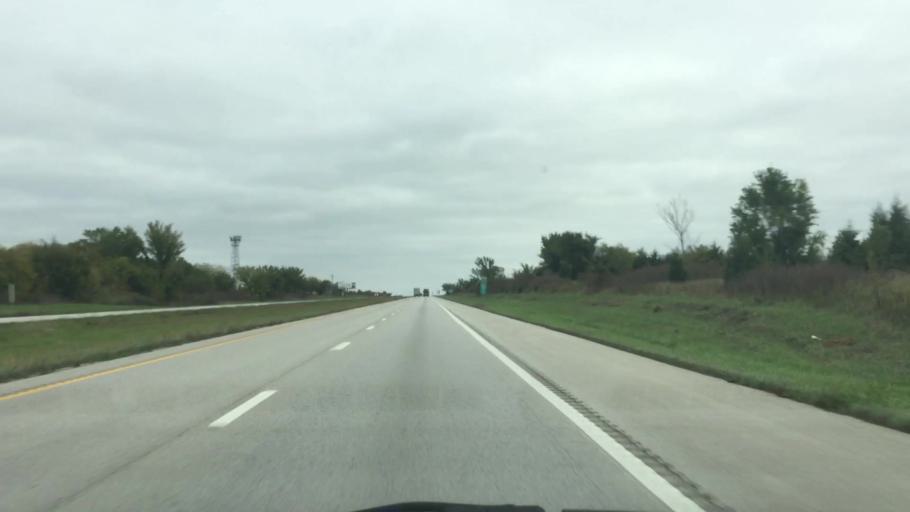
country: US
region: Missouri
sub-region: Clinton County
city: Cameron
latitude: 39.8270
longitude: -94.1884
